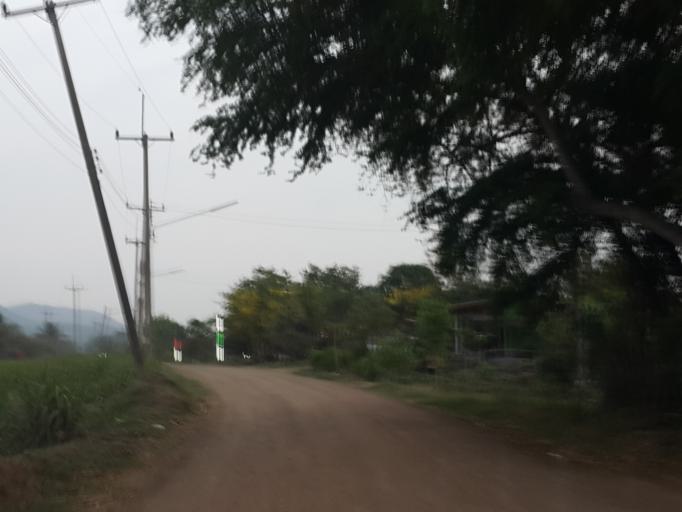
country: TH
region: Suphan Buri
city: Dan Chang
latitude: 14.9209
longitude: 99.6425
